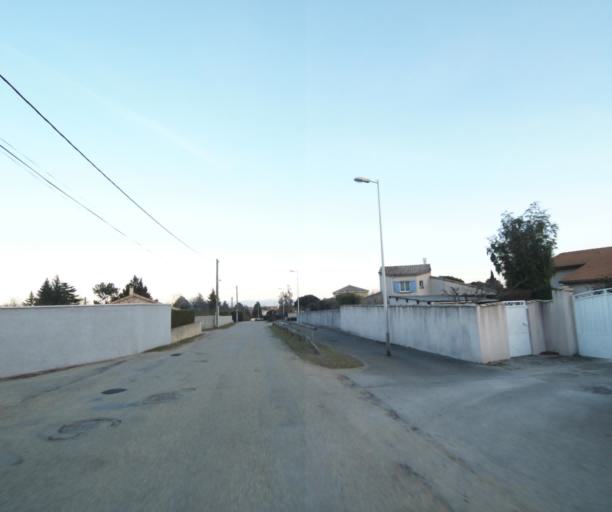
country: FR
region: Rhone-Alpes
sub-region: Departement de l'Ardeche
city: Davezieux
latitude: 45.2593
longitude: 4.7132
